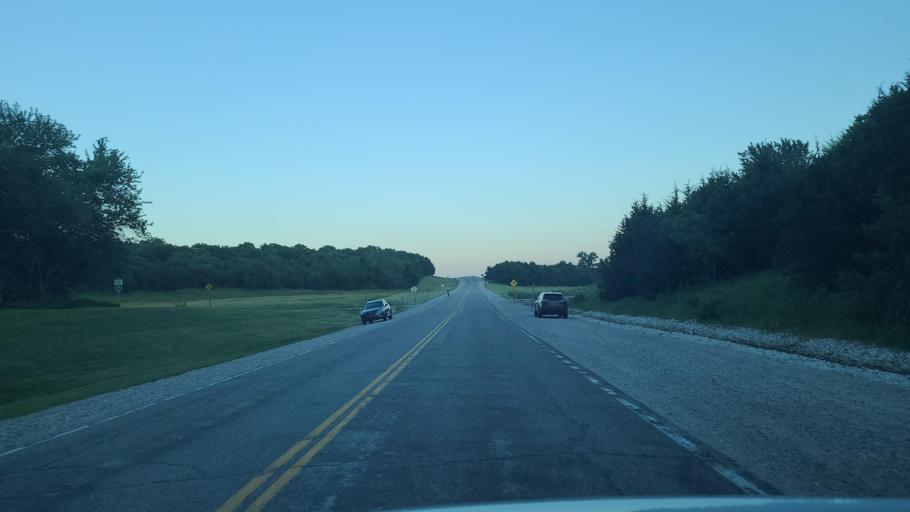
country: US
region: Kansas
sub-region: Douglas County
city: Lawrence
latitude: 38.9410
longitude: -95.3362
